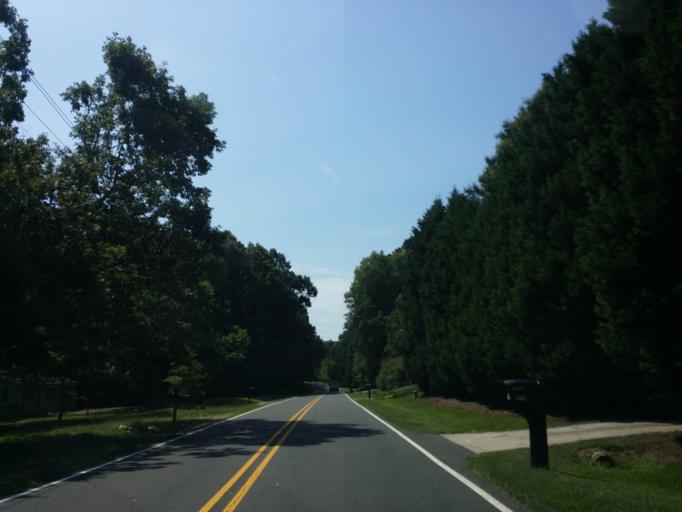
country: US
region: North Carolina
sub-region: Wake County
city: Cary
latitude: 35.8964
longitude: -78.7272
